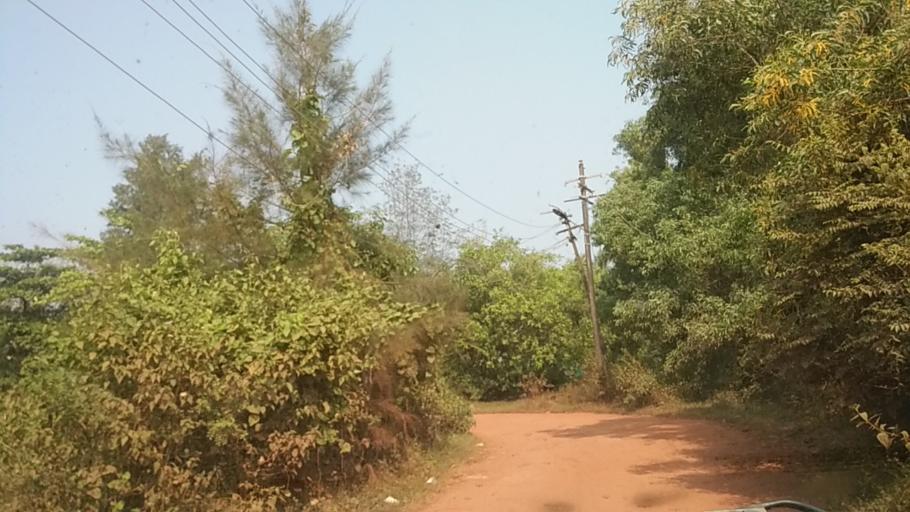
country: IN
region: Goa
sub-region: South Goa
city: Colva
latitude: 15.2897
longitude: 73.9110
